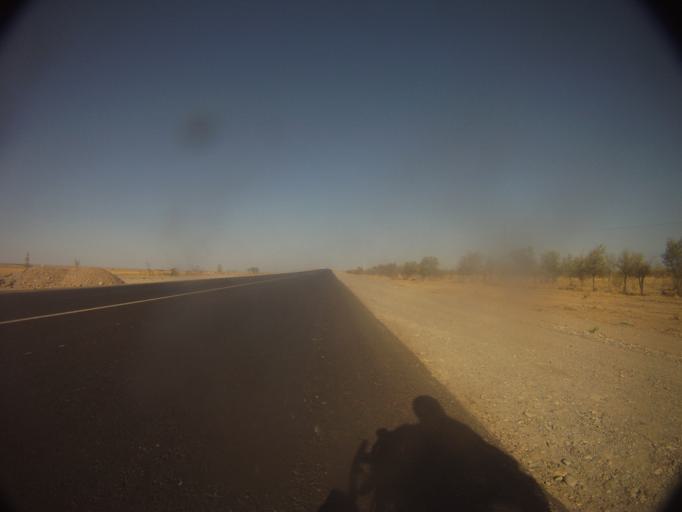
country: KZ
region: Zhambyl
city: Sarykemer
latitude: 42.9781
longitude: 71.5743
